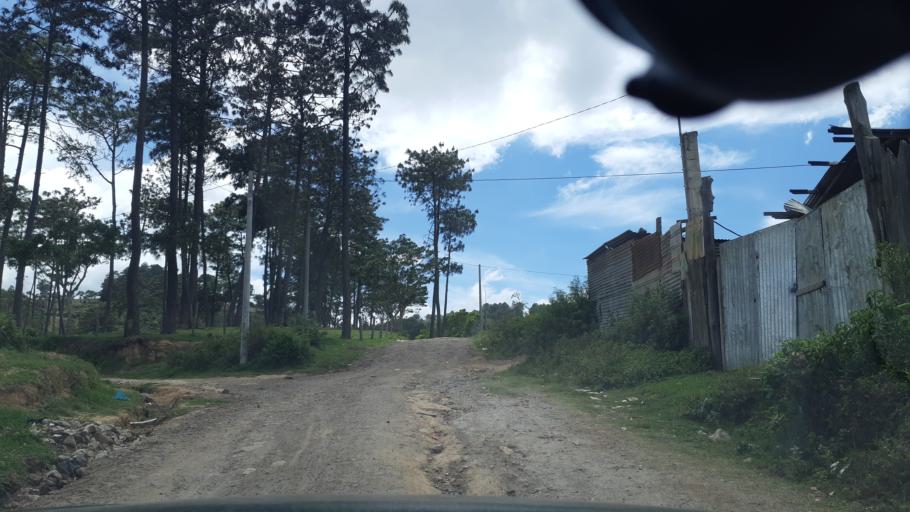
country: GT
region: Chimaltenango
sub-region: Municipio de Chimaltenango
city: Chimaltenango
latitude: 14.6608
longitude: -90.8457
